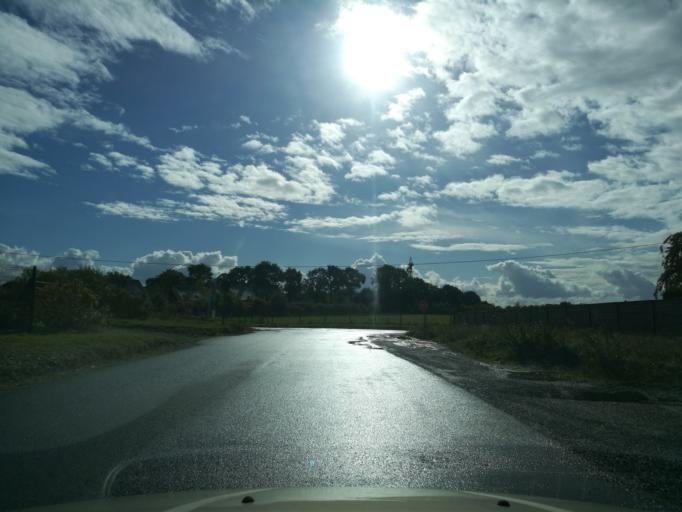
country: FR
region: Brittany
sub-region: Departement d'Ille-et-Vilaine
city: Pleumeleuc
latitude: 48.1831
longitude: -1.9284
